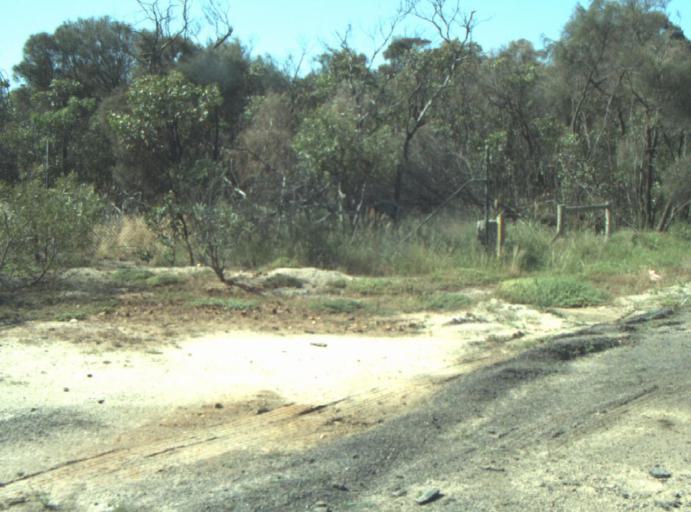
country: AU
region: Victoria
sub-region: Greater Geelong
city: Lara
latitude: -37.9363
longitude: 144.3935
